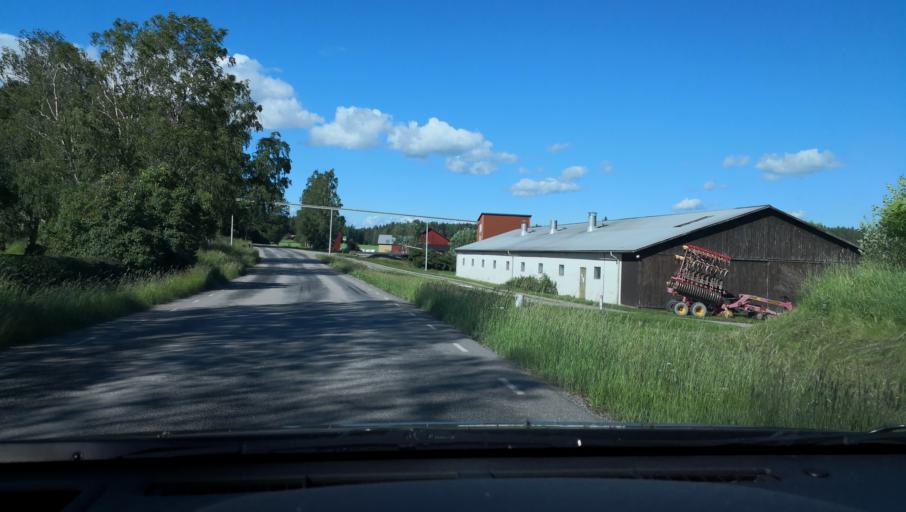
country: SE
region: Soedermanland
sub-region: Eskilstuna Kommun
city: Arla
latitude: 59.3201
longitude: 16.6087
